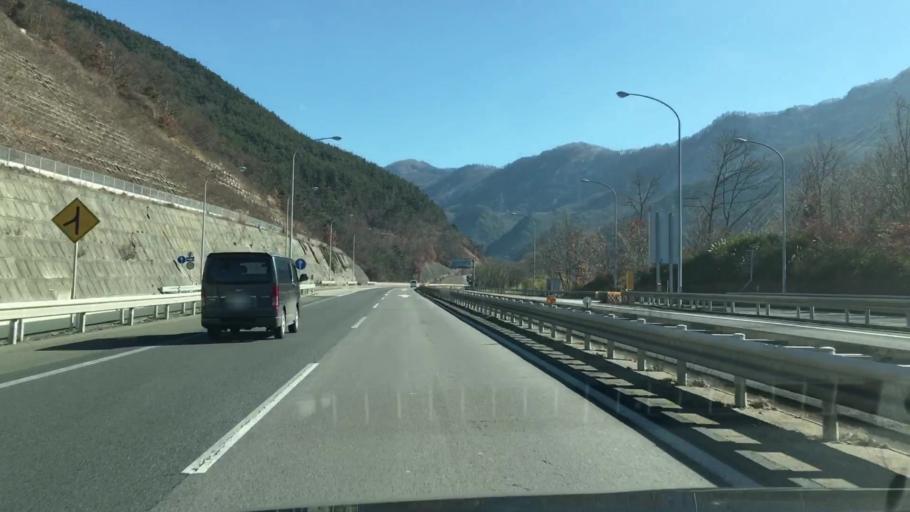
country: JP
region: Nagano
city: Ueda
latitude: 36.4444
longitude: 138.2102
